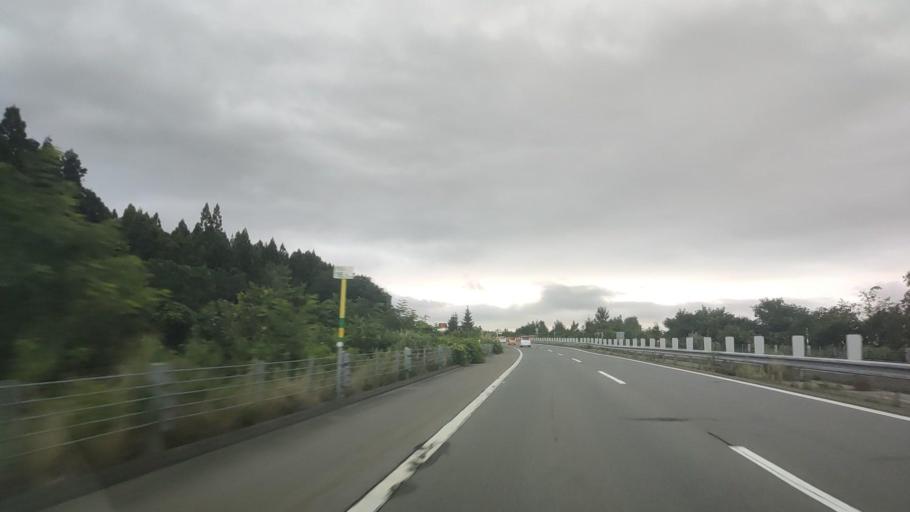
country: JP
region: Hokkaido
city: Nanae
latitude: 41.9050
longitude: 140.6978
